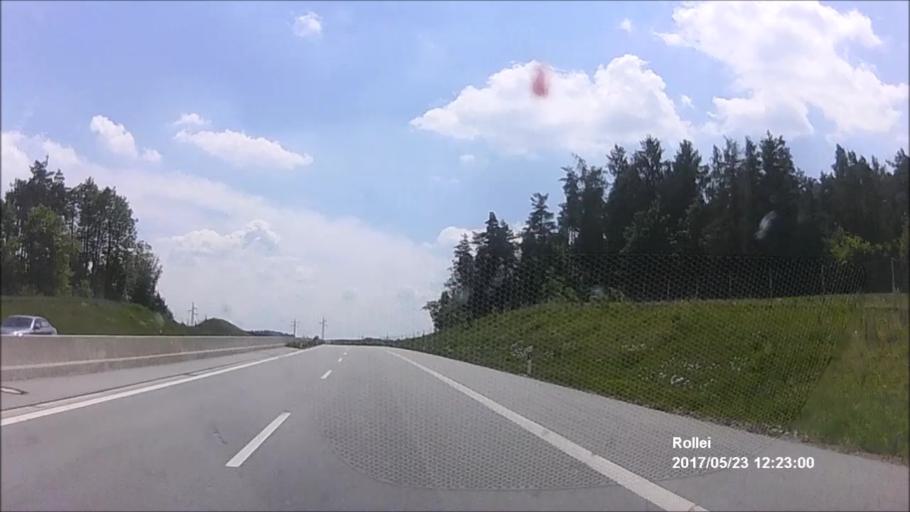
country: DE
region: Bavaria
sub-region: Lower Bavaria
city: Ergoldsbach
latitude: 48.6974
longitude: 12.1790
